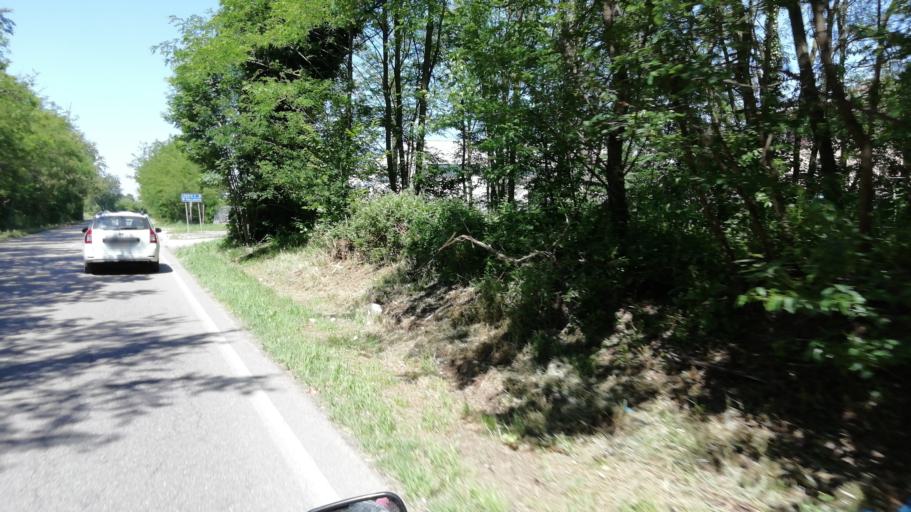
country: IT
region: Lombardy
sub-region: Provincia di Varese
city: Lonate Pozzolo
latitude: 45.5980
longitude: 8.7425
